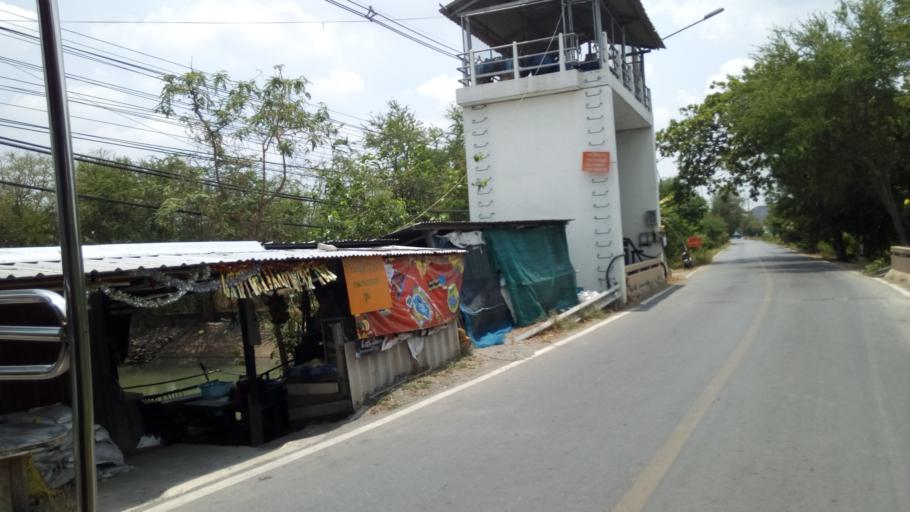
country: TH
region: Pathum Thani
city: Sam Khok
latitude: 14.0833
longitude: 100.5218
